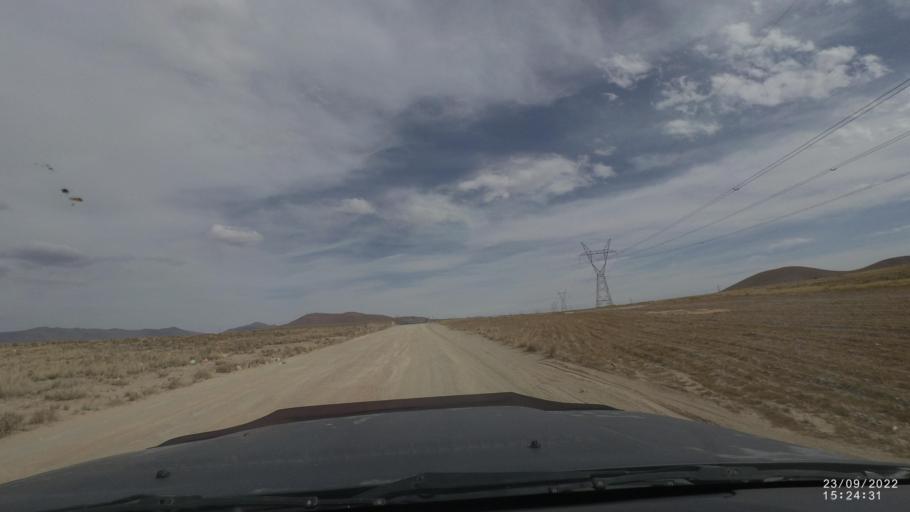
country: BO
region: Oruro
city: Oruro
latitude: -17.9356
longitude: -67.0406
